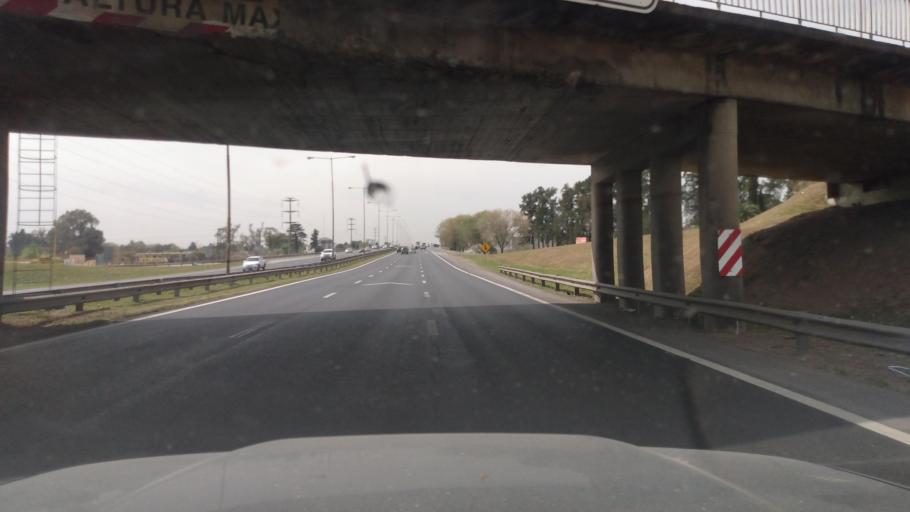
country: AR
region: Buenos Aires
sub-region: Partido de Pilar
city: Pilar
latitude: -34.4529
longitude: -58.9298
